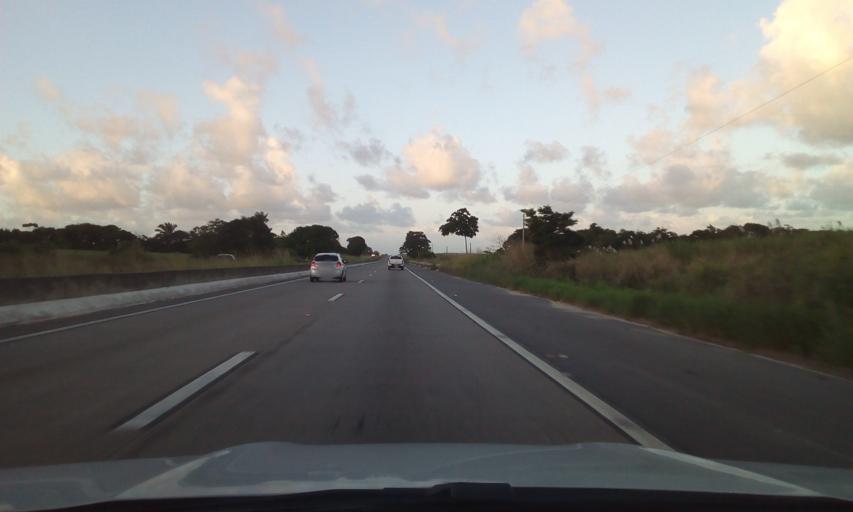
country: BR
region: Pernambuco
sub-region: Itapissuma
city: Itapissuma
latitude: -7.7177
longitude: -34.9383
